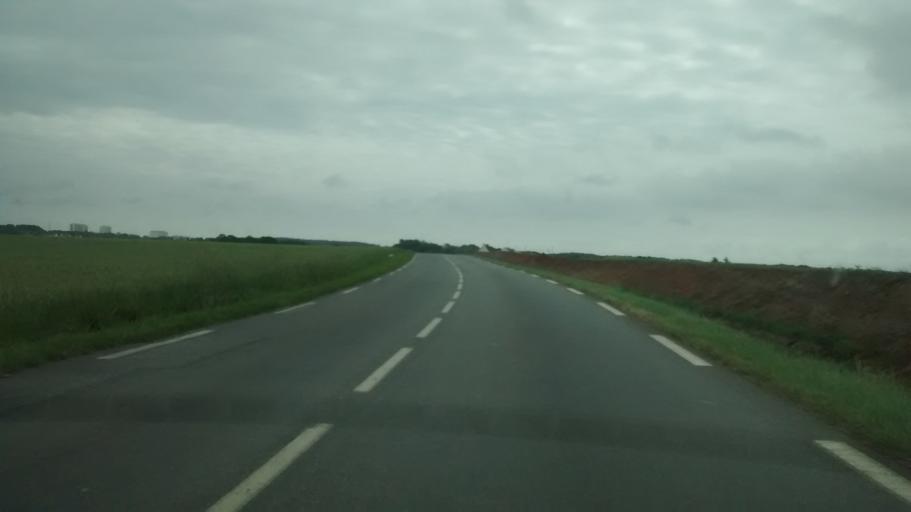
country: FR
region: Brittany
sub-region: Departement du Morbihan
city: Queven
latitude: 47.7607
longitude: -3.4237
